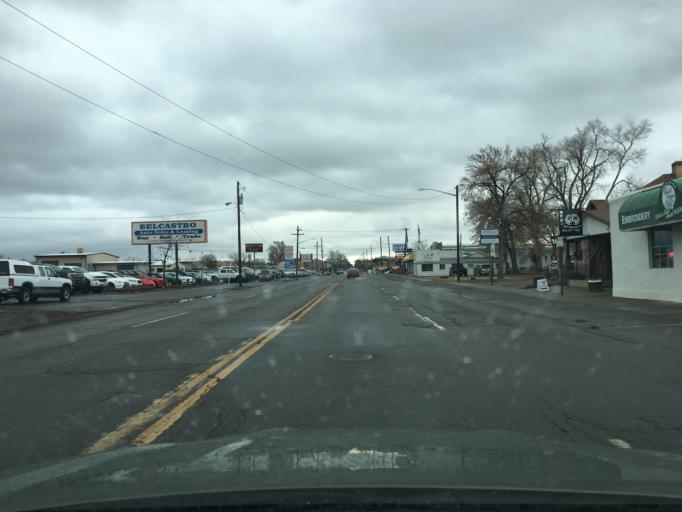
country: US
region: Colorado
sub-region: Mesa County
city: Grand Junction
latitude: 39.0749
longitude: -108.5708
